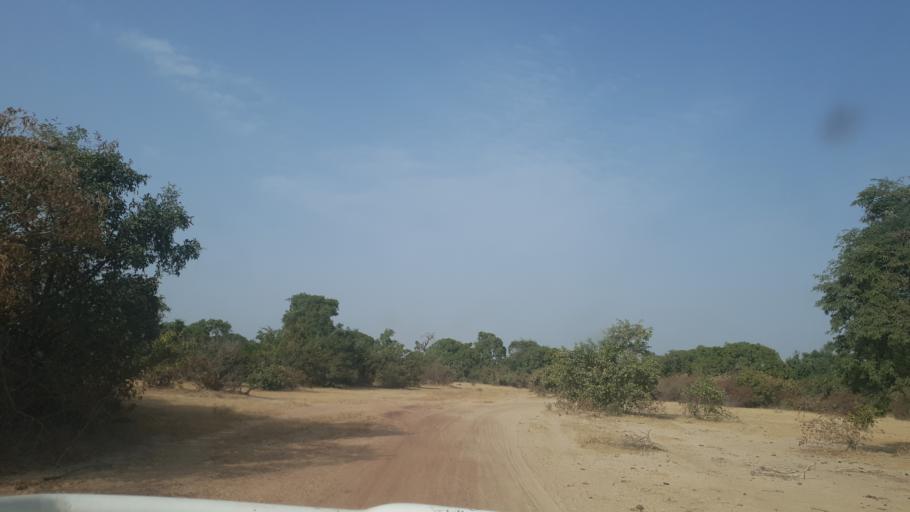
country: ML
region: Segou
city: Baroueli
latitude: 13.3702
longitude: -6.9158
